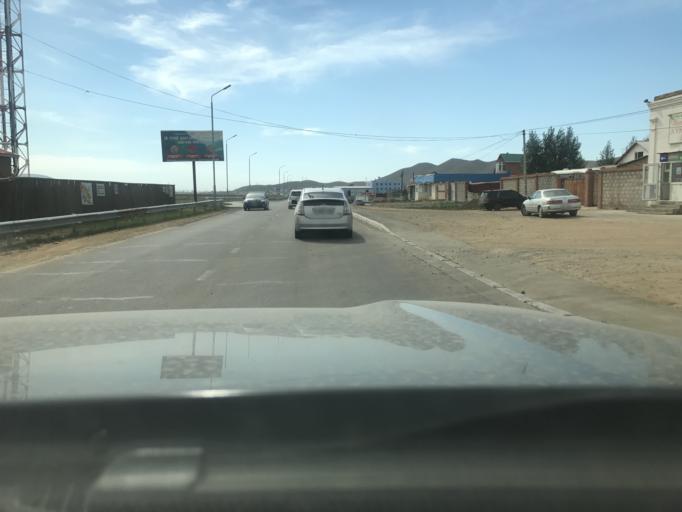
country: MN
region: Ulaanbaatar
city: Ulaanbaatar
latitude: 47.9156
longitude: 107.0950
